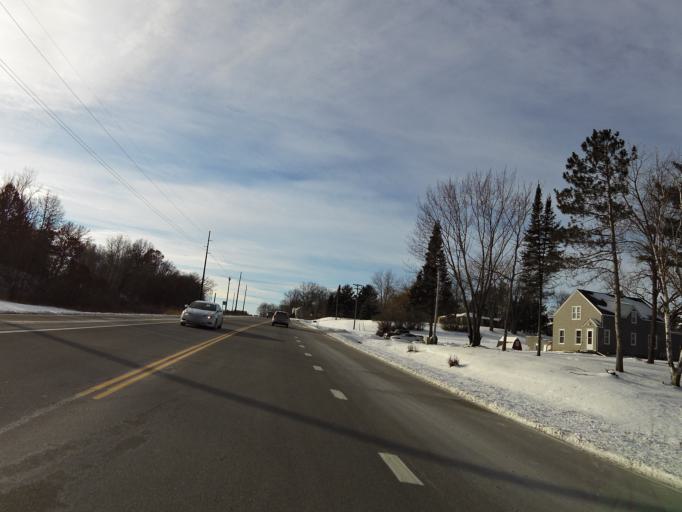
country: US
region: Minnesota
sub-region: Dakota County
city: Eagan
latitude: 44.8011
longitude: -93.1059
